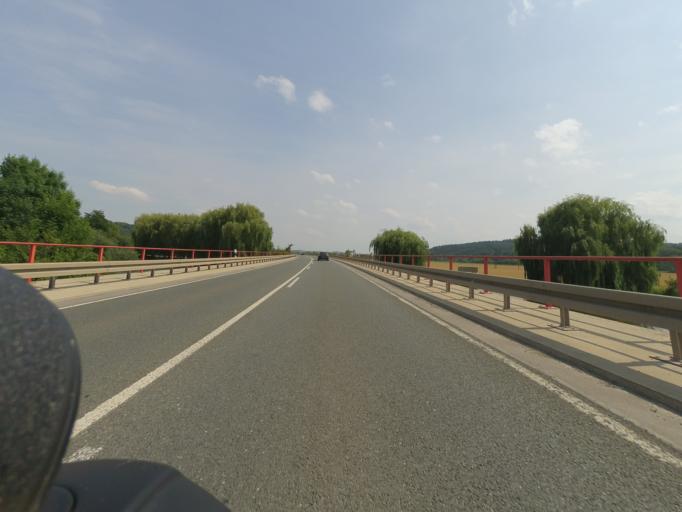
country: DE
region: Thuringia
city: Bad Kostritz
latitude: 50.9290
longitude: 12.0271
